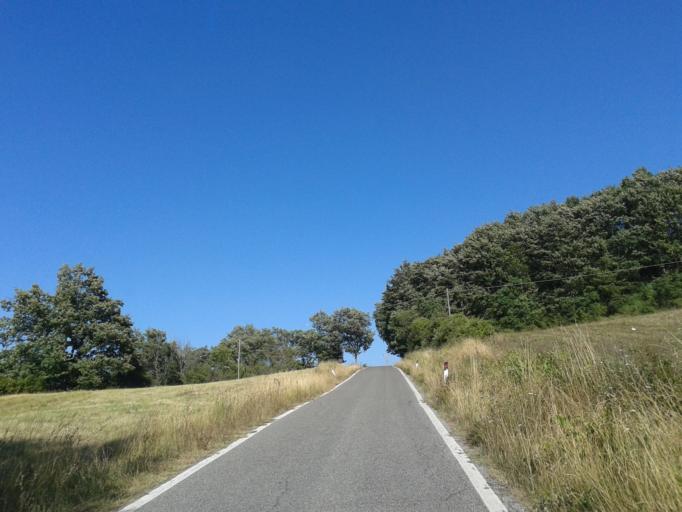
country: IT
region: Tuscany
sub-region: Province of Pisa
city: Chianni
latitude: 43.4550
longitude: 10.6273
